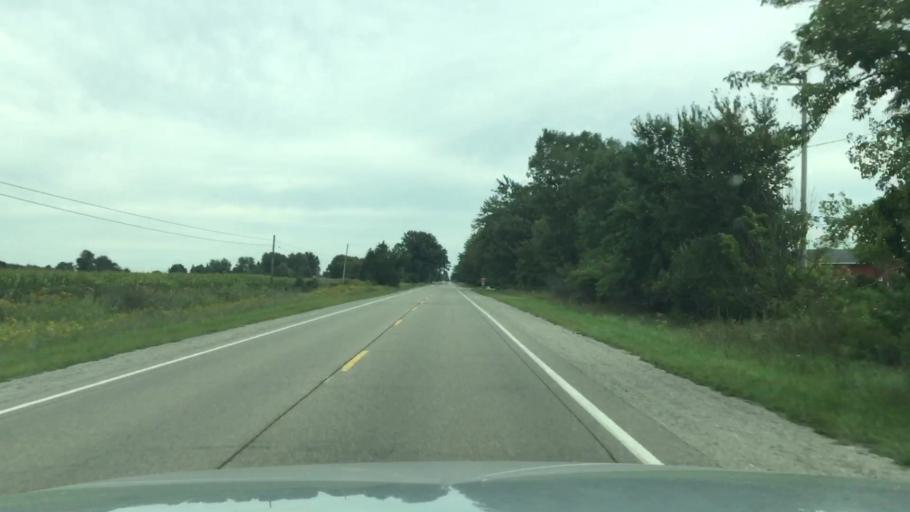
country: US
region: Michigan
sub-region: Genesee County
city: Swartz Creek
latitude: 42.9570
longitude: -83.8981
